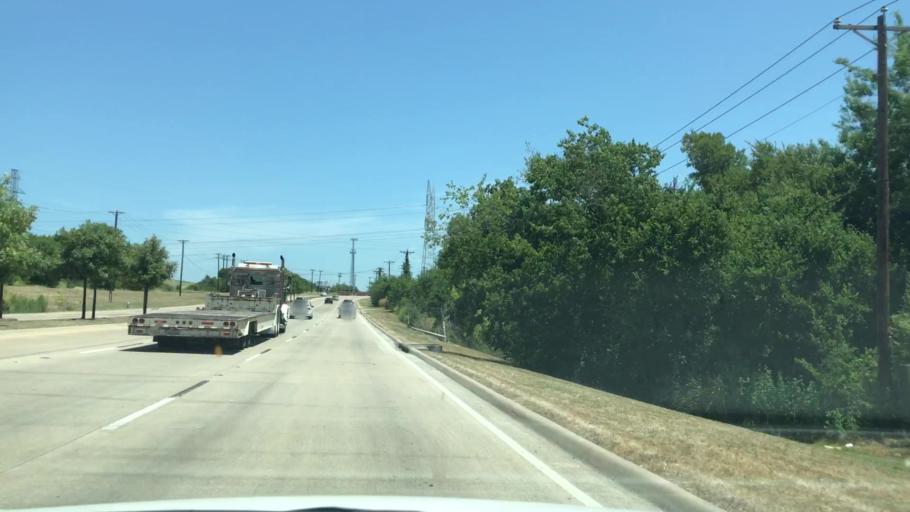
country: US
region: Texas
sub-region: Collin County
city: Wylie
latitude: 33.0200
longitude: -96.5268
